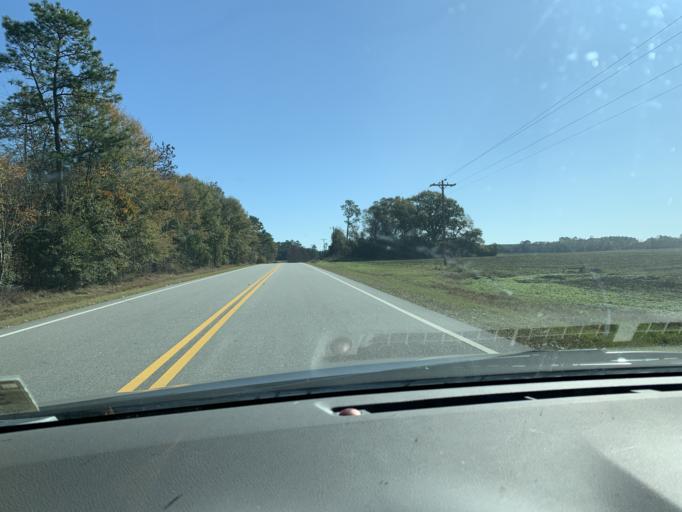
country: US
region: Georgia
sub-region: Ben Hill County
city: Fitzgerald
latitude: 31.7034
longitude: -83.1528
